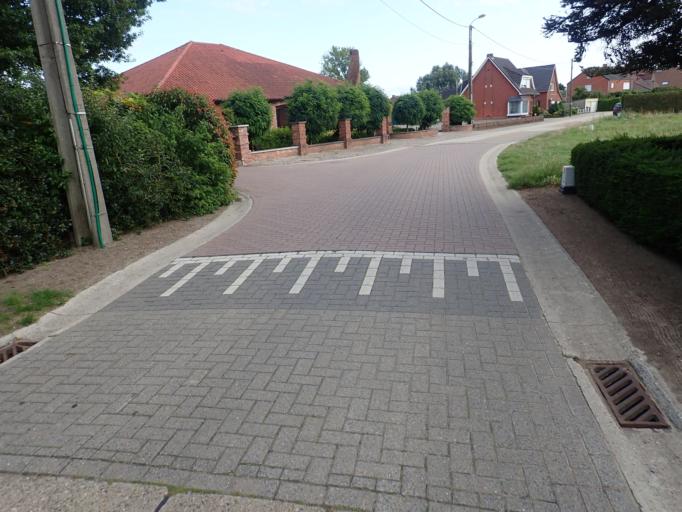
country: BE
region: Flanders
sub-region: Provincie Antwerpen
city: Oostmalle
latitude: 51.2940
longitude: 4.7776
